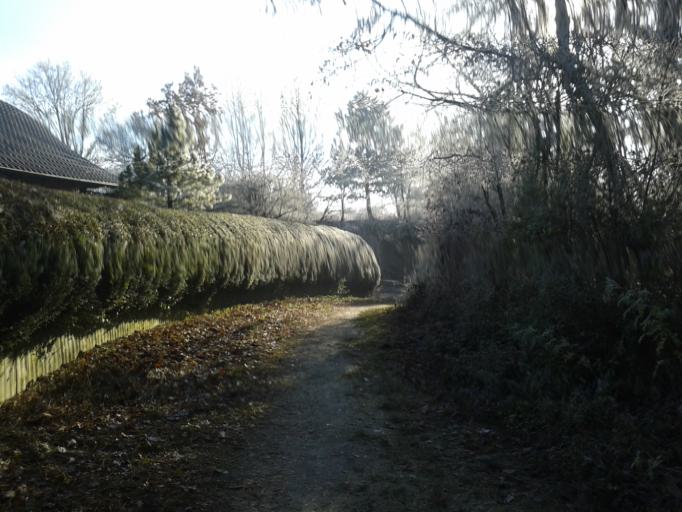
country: DE
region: Bavaria
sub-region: Swabia
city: Neu-Ulm
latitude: 48.4316
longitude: 10.0139
